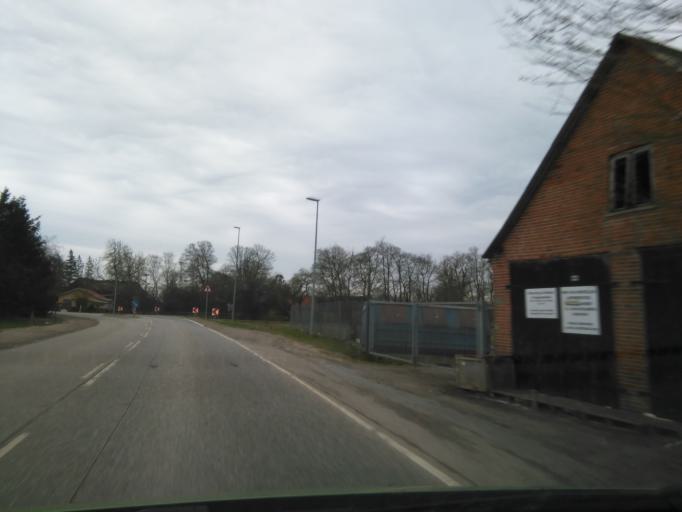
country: DK
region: Central Jutland
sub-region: Randers Kommune
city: Spentrup
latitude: 56.5578
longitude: 10.0010
